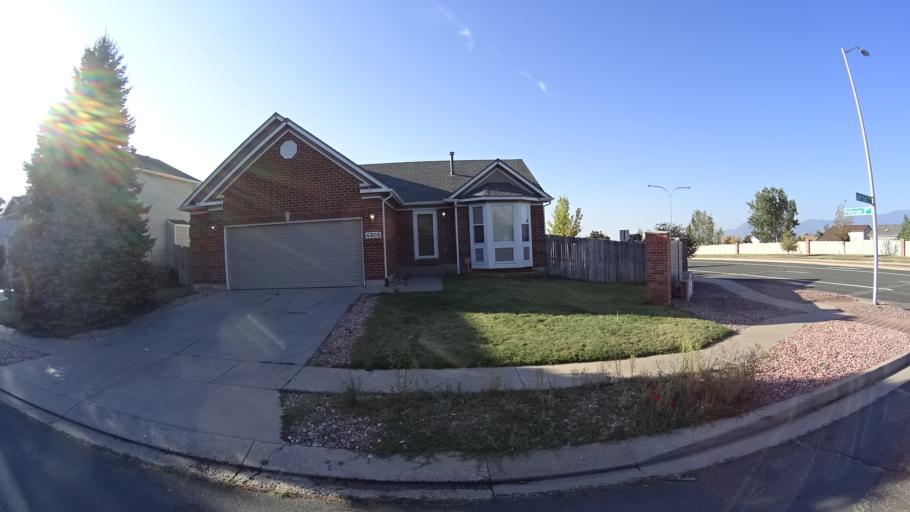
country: US
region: Colorado
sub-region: El Paso County
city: Cimarron Hills
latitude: 38.8927
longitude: -104.7016
